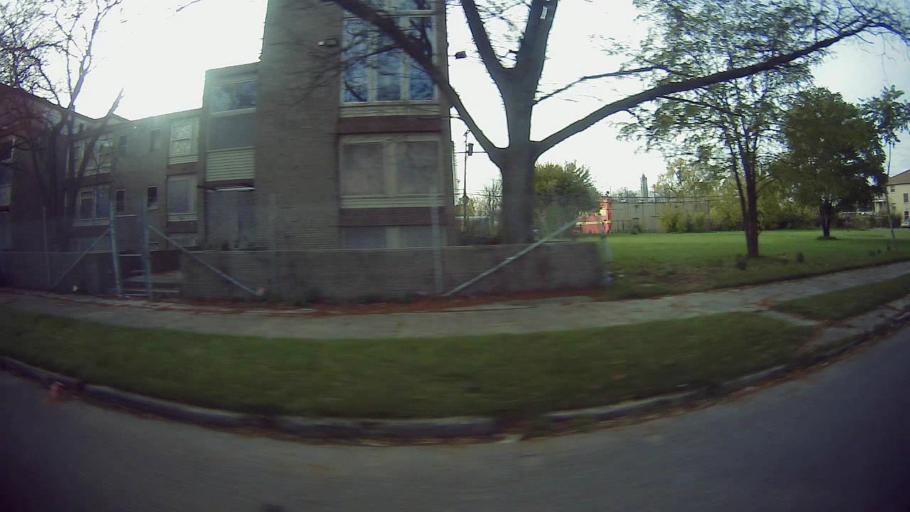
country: US
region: Michigan
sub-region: Wayne County
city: Highland Park
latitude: 42.4185
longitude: -83.1141
